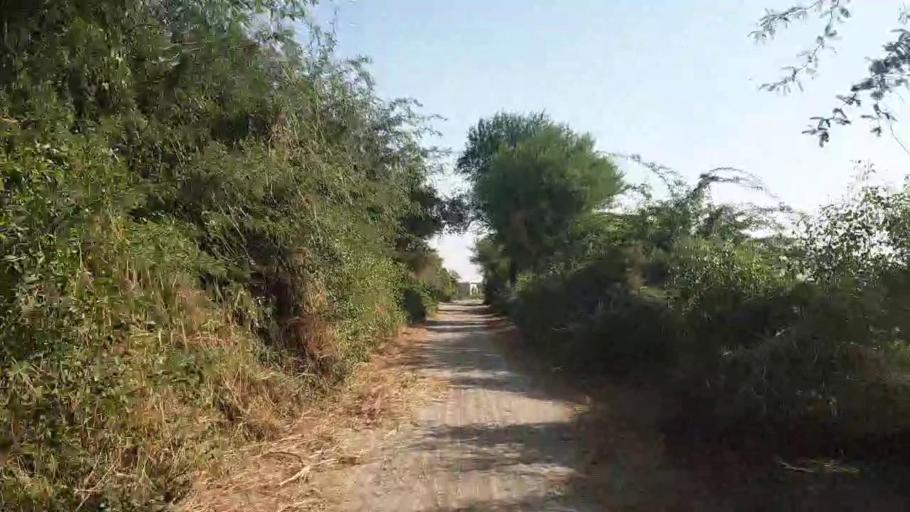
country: PK
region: Sindh
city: Matli
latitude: 25.0210
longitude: 68.7381
